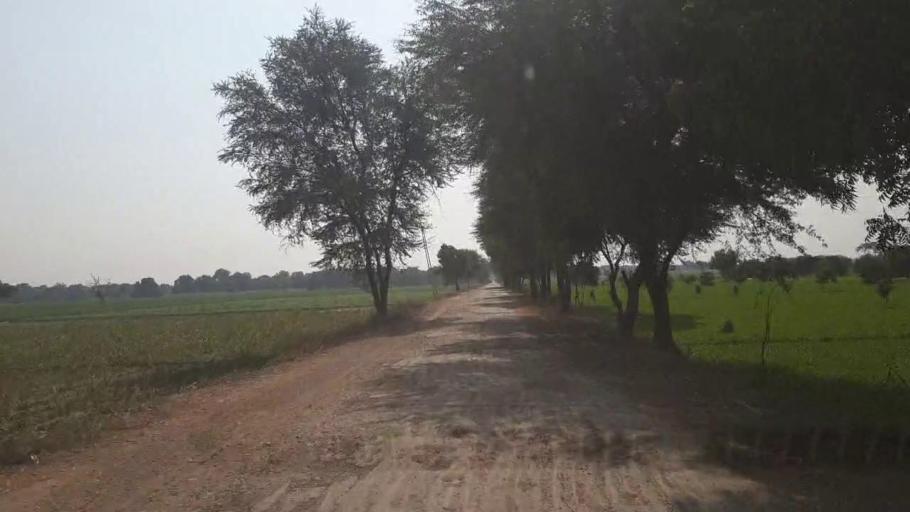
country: PK
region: Sindh
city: Tando Allahyar
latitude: 25.4851
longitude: 68.8261
